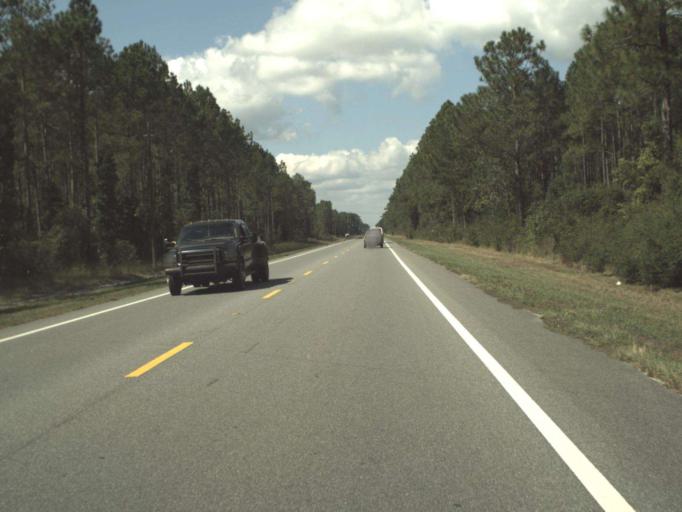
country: US
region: Florida
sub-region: Walton County
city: Freeport
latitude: 30.4827
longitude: -86.1031
